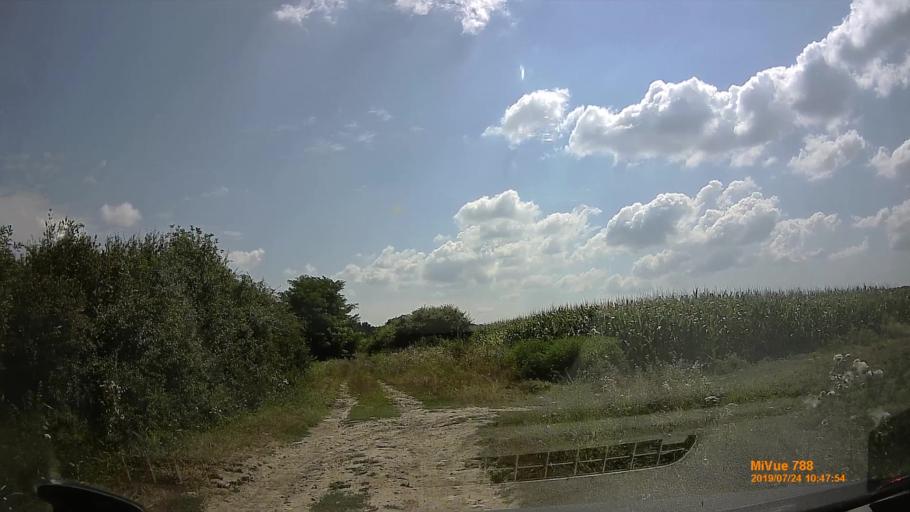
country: UA
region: Zakarpattia
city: Berehove
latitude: 48.1951
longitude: 22.5659
